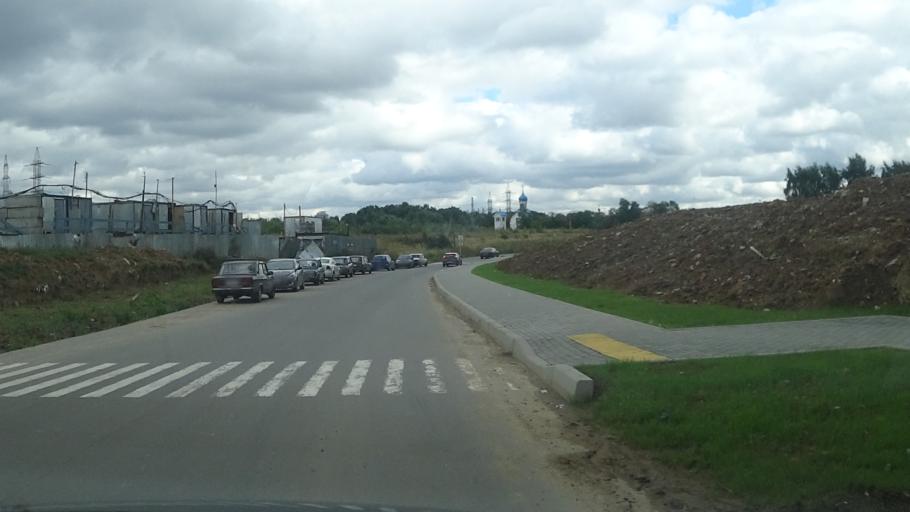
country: RU
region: Moskovskaya
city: Vostryakovo
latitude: 55.6561
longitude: 37.4290
